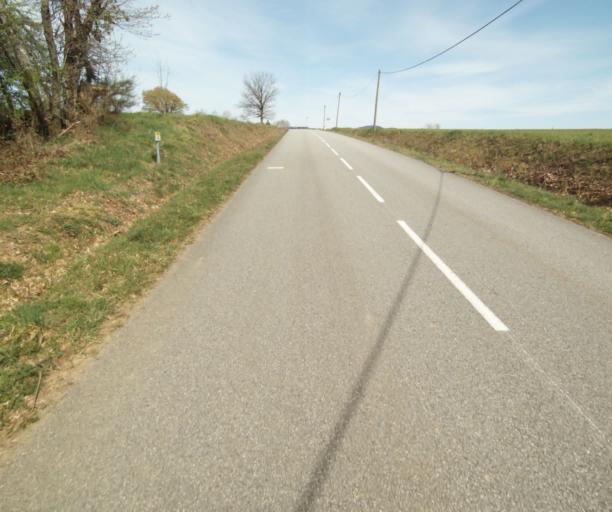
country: FR
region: Limousin
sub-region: Departement de la Correze
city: Correze
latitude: 45.3849
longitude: 1.8066
